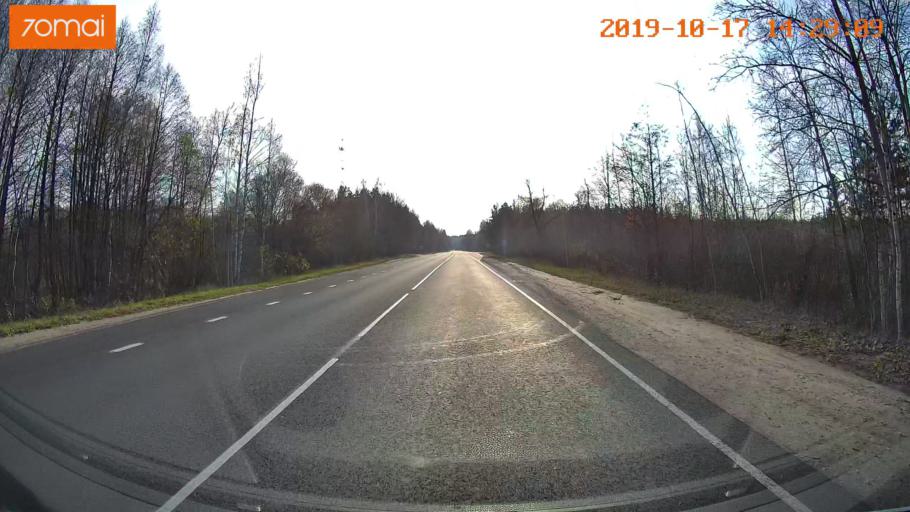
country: RU
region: Rjazan
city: Solotcha
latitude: 54.9642
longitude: 39.9452
